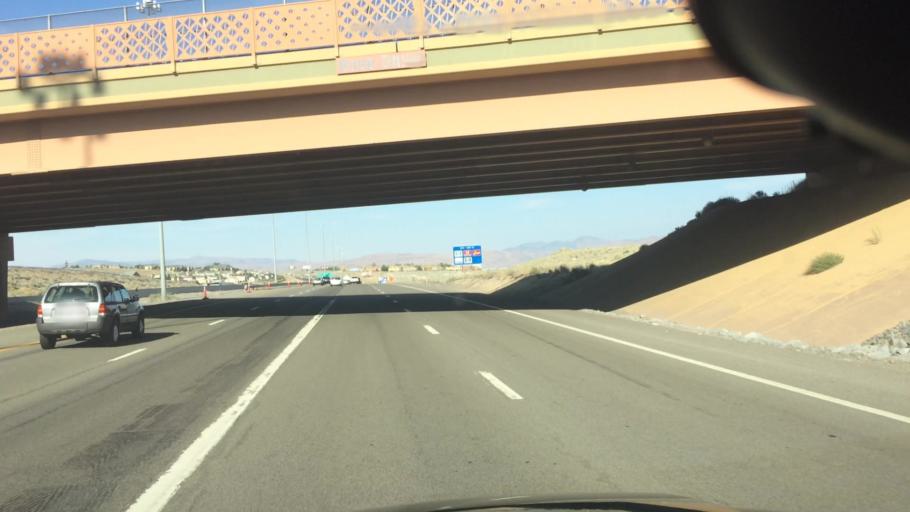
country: US
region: Nevada
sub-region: Washoe County
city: Mogul
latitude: 39.5157
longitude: -119.8875
